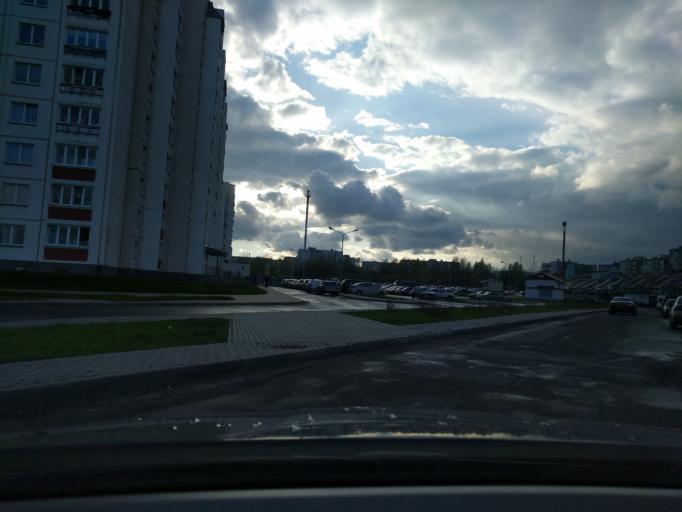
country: BY
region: Minsk
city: Novoye Medvezhino
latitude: 53.8947
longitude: 27.4626
